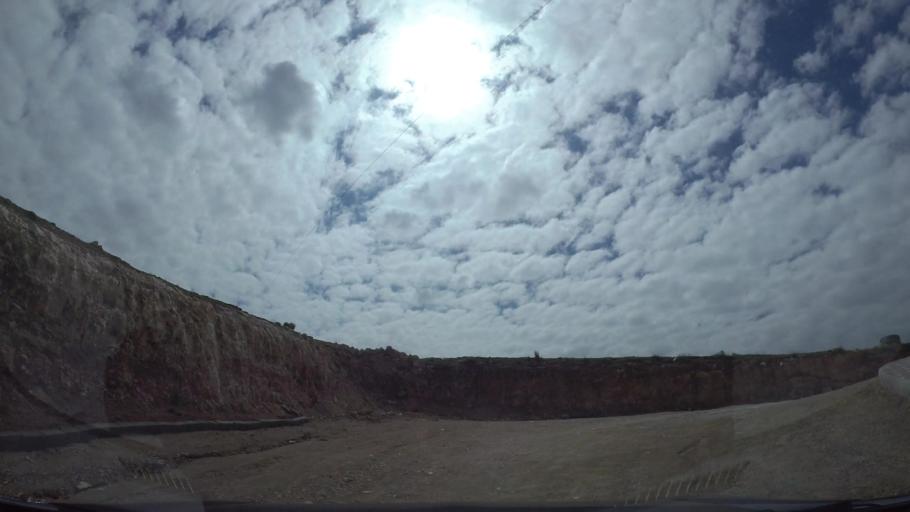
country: JO
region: Amman
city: Al Jubayhah
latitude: 32.0025
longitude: 35.9145
